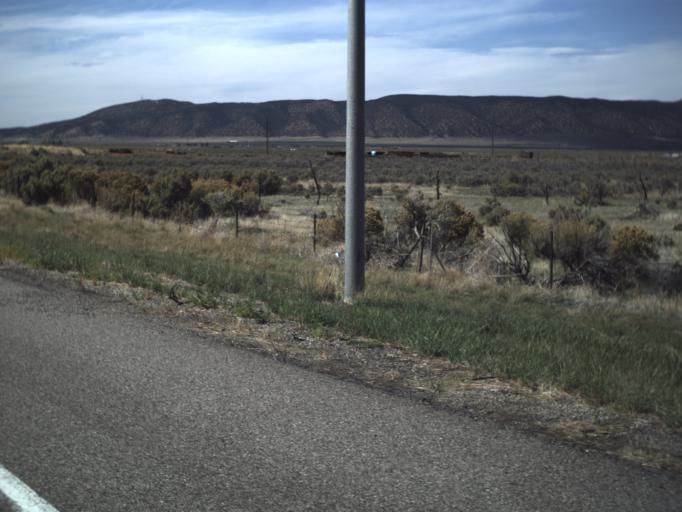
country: US
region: Utah
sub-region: Iron County
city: Parowan
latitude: 37.8405
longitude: -112.8662
